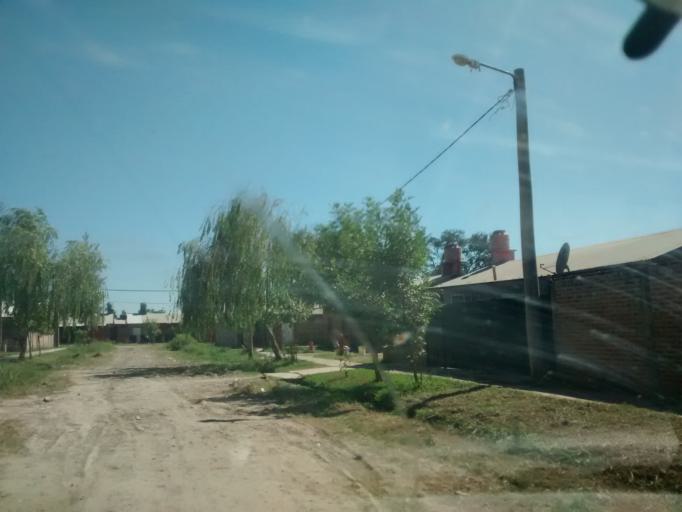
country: AR
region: Chaco
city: Fontana
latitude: -27.4013
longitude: -58.9949
